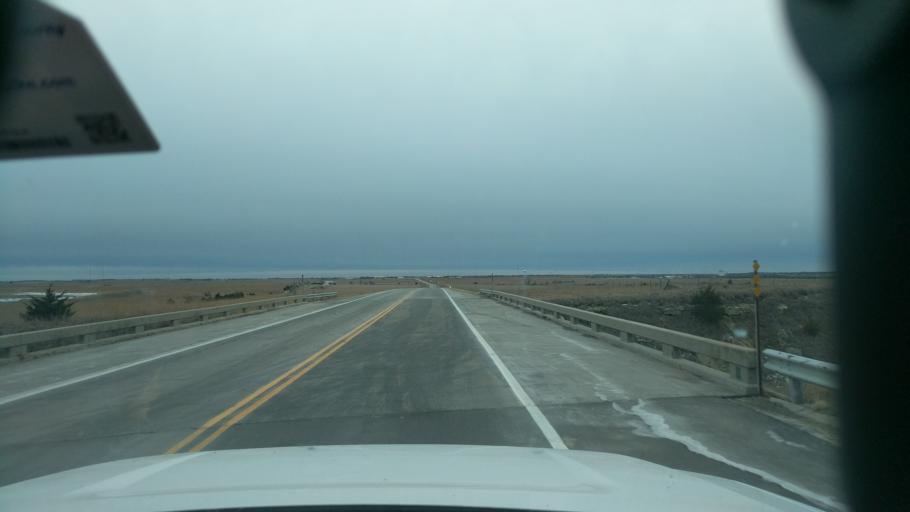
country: US
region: Kansas
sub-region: Dickinson County
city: Herington
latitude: 38.7087
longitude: -96.9288
